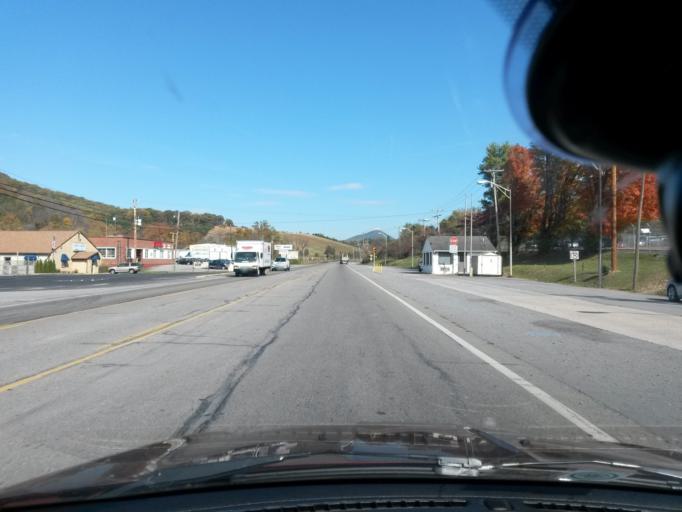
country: US
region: Virginia
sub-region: Botetourt County
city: Cloverdale
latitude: 37.3592
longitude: -79.9257
